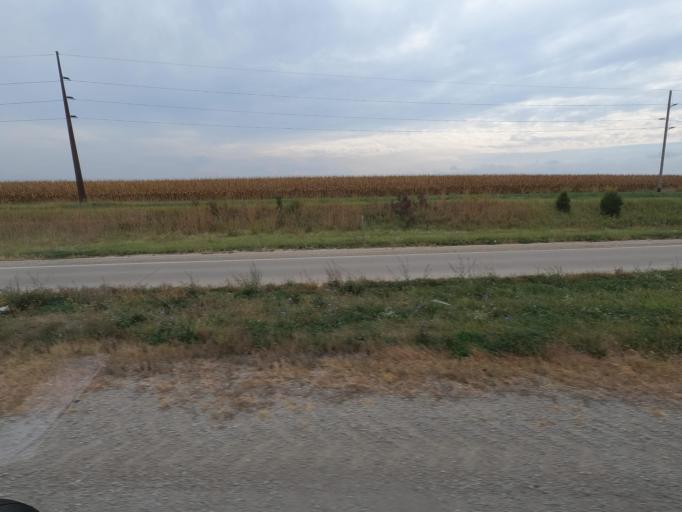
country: US
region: Iowa
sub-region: Marion County
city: Pella
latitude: 41.3893
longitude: -92.8660
